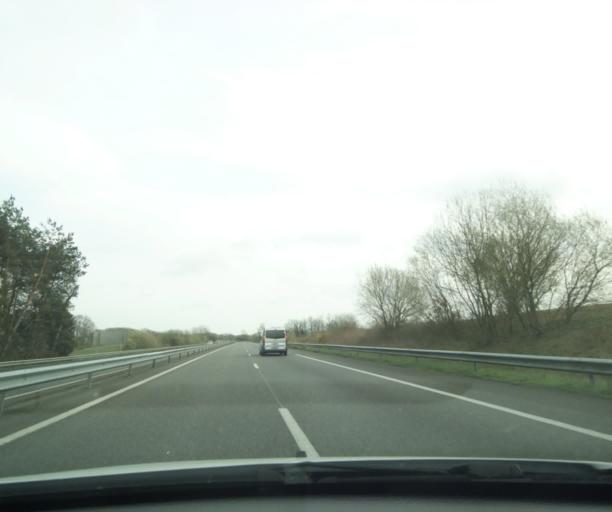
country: FR
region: Aquitaine
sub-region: Departement des Landes
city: Peyrehorade
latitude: 43.5200
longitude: -1.1322
